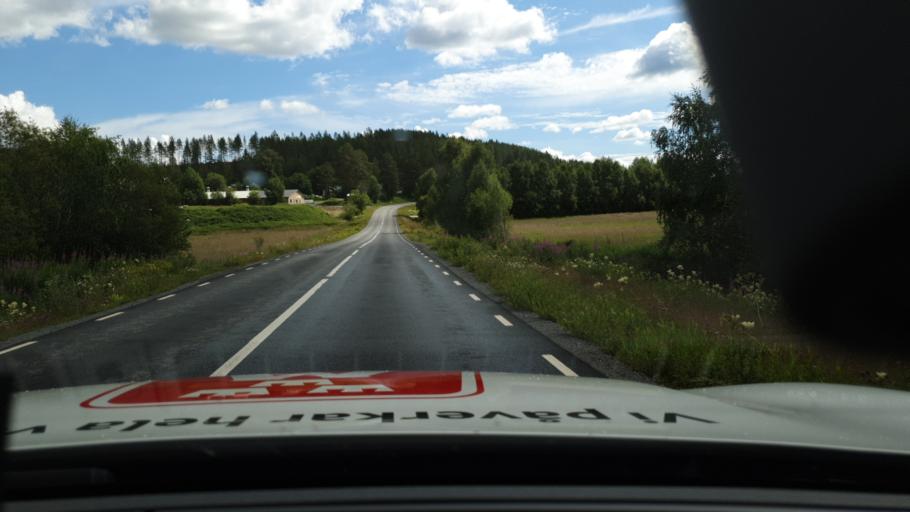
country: SE
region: Norrbotten
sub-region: Bodens Kommun
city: Saevast
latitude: 65.8312
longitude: 21.8776
